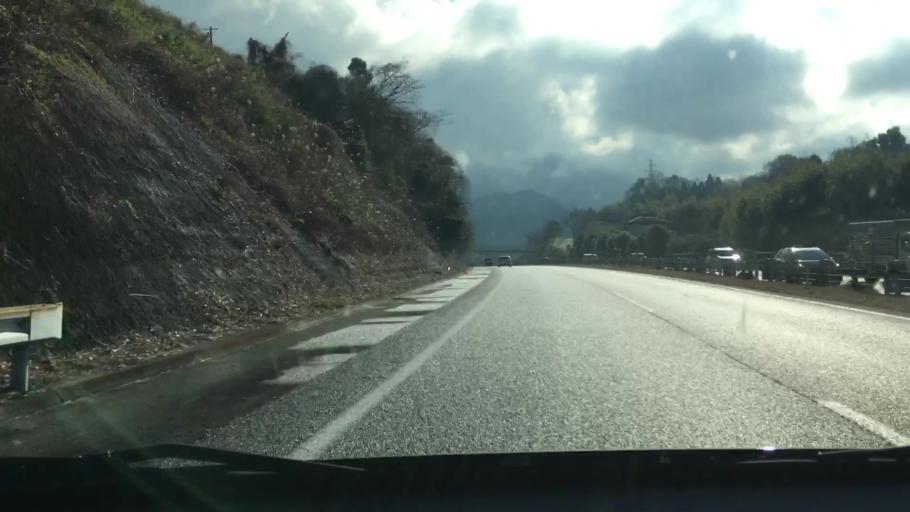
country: JP
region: Kumamoto
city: Matsubase
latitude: 32.5579
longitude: 130.6958
